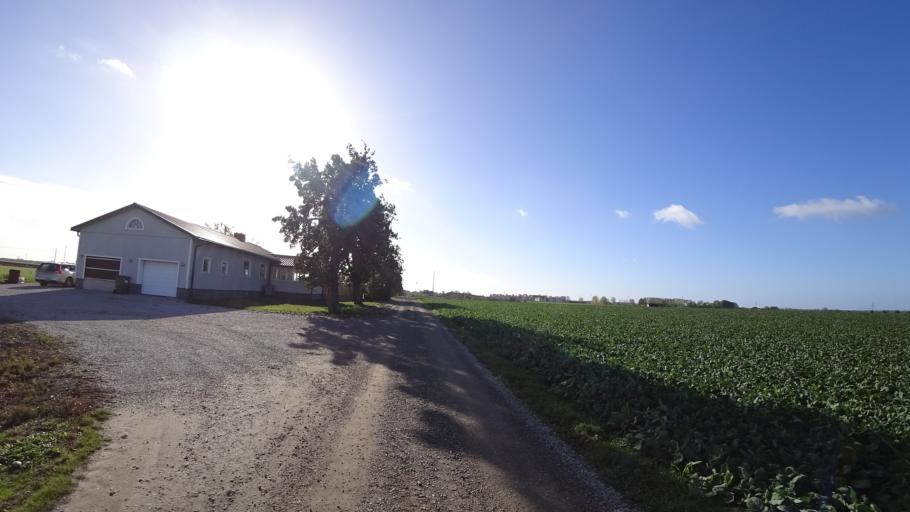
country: SE
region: Skane
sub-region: Staffanstorps Kommun
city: Hjaerup
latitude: 55.6820
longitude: 13.1456
